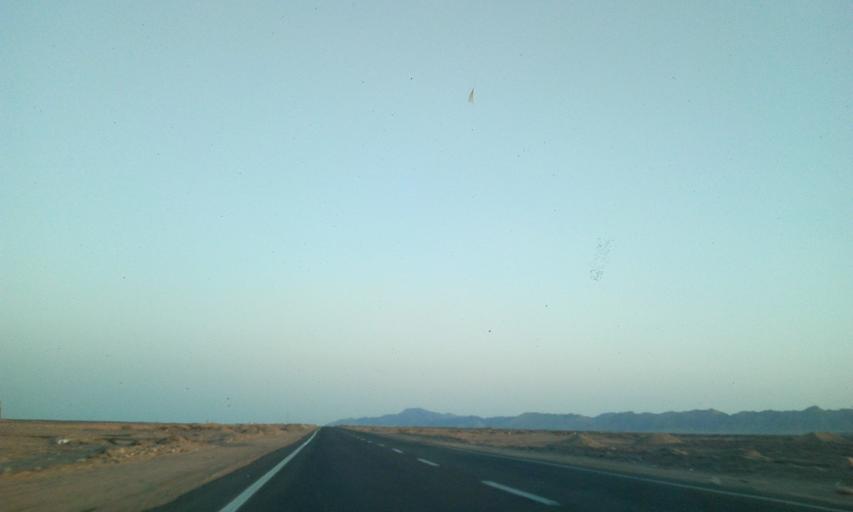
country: EG
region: Red Sea
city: El Gouna
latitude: 27.6087
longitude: 33.5061
